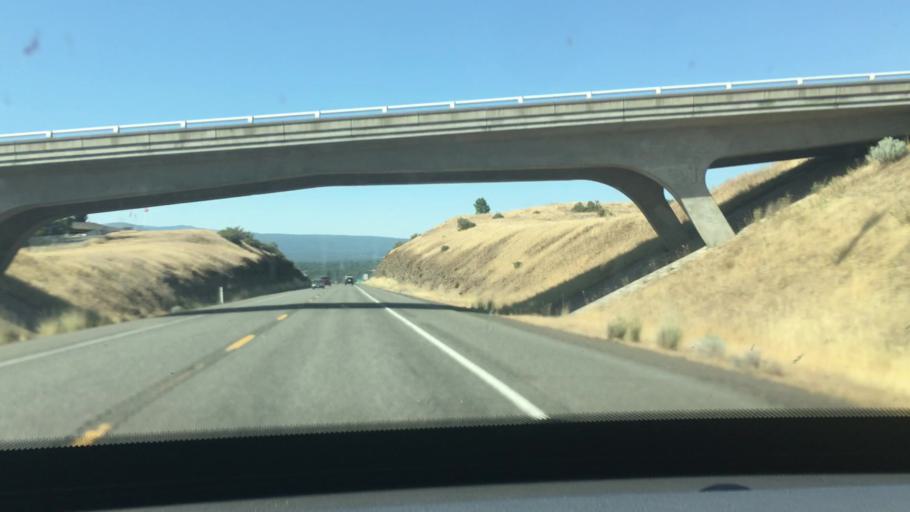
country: US
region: Washington
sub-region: Klickitat County
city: Goldendale
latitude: 45.8181
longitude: -120.8059
